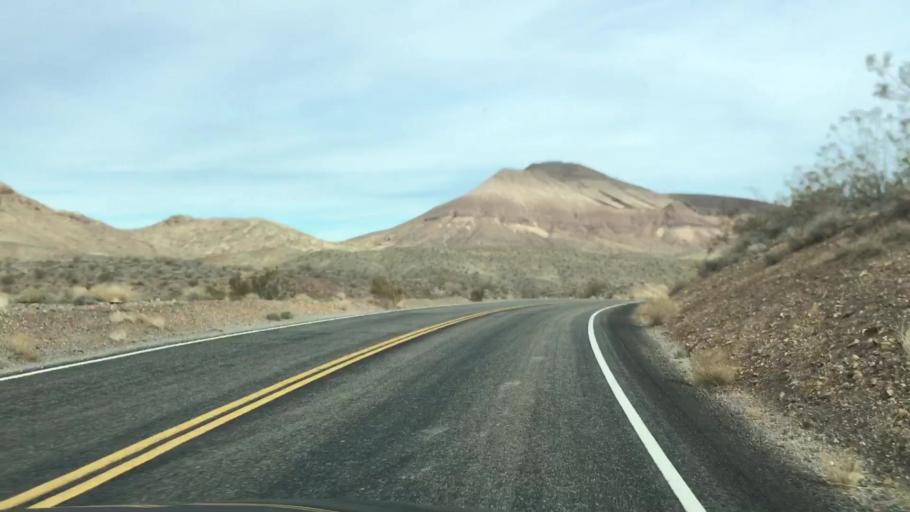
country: US
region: Nevada
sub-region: Nye County
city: Beatty
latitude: 36.7890
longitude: -116.9321
